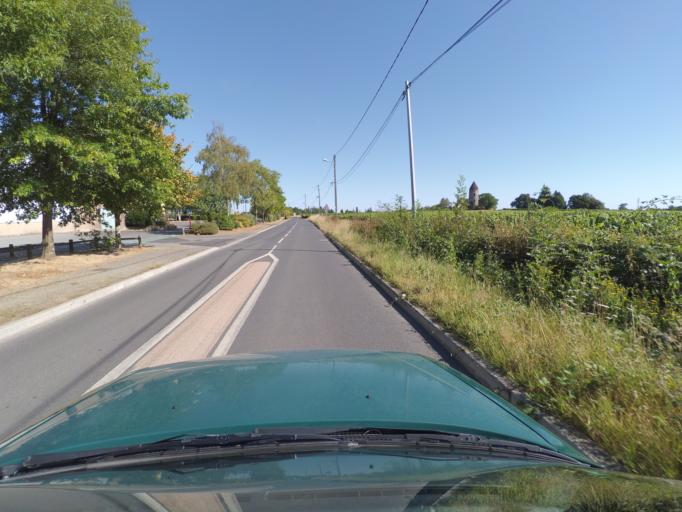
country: FR
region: Pays de la Loire
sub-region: Departement de la Loire-Atlantique
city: Maisdon-sur-Sevre
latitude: 47.0958
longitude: -1.3812
